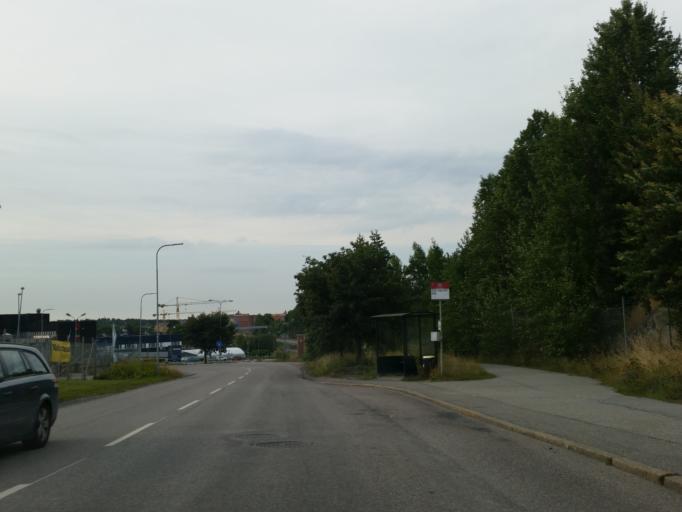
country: SE
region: Stockholm
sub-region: Jarfalla Kommun
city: Jakobsberg
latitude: 59.4101
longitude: 17.8391
